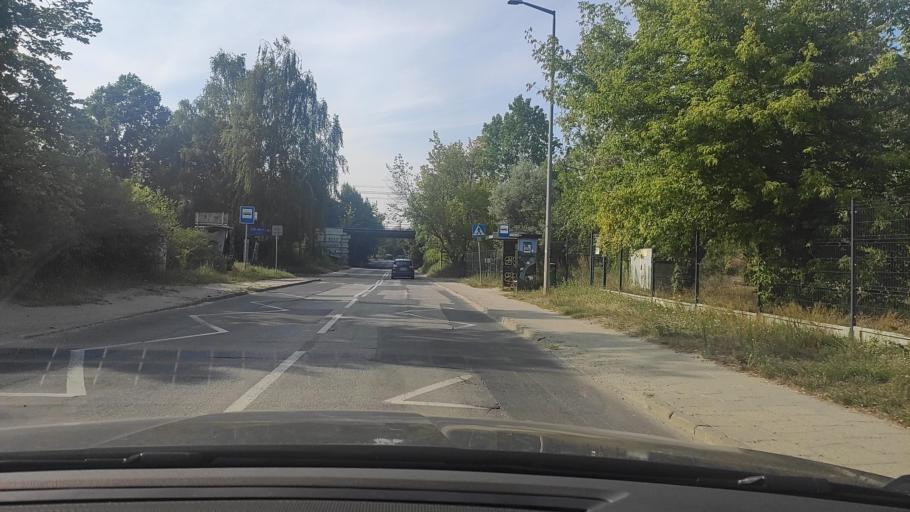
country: PL
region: Greater Poland Voivodeship
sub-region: Powiat poznanski
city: Swarzedz
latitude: 52.3888
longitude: 17.0257
